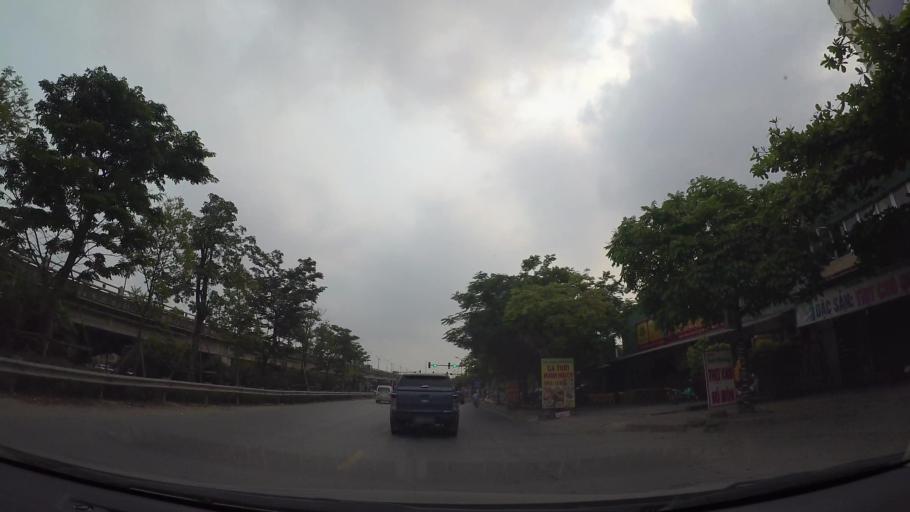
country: VN
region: Ha Noi
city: Trau Quy
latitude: 21.0051
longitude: 105.9115
